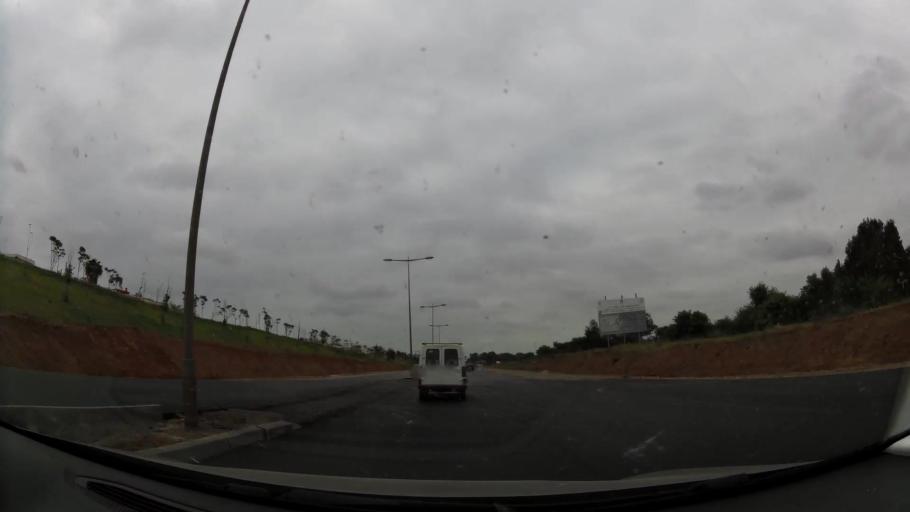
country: MA
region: Rabat-Sale-Zemmour-Zaer
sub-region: Rabat
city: Rabat
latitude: 33.9674
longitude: -6.8192
